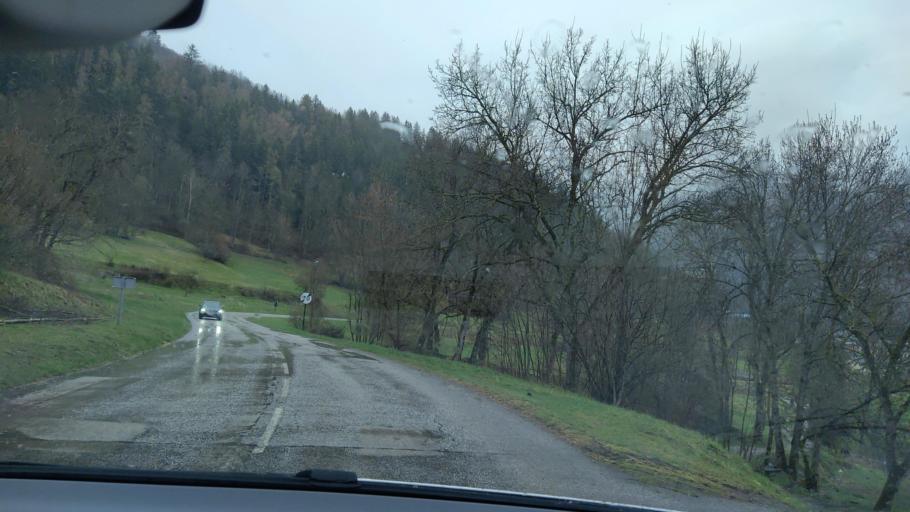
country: FR
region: Rhone-Alpes
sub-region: Departement de la Savoie
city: Bourg-Saint-Maurice
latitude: 45.5772
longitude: 6.7437
